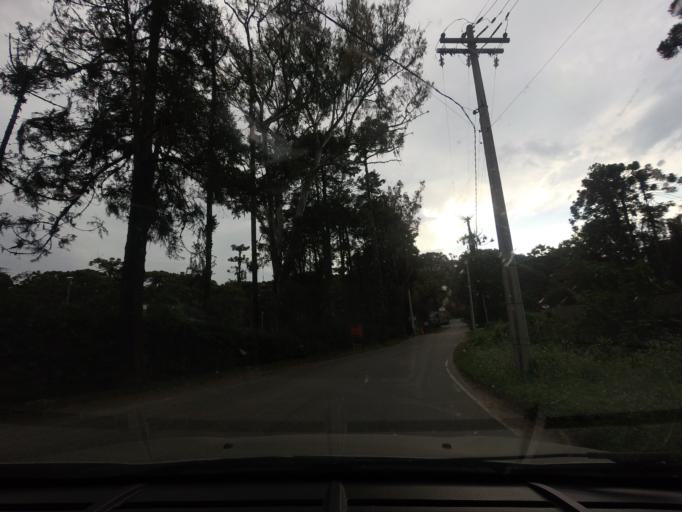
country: BR
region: Sao Paulo
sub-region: Campos Do Jordao
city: Campos do Jordao
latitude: -22.6964
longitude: -45.5134
